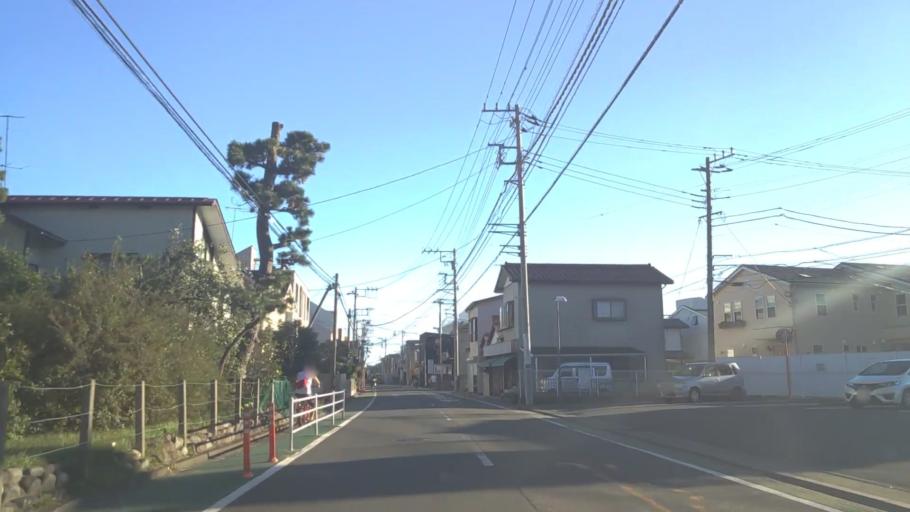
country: JP
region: Kanagawa
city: Chigasaki
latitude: 35.3297
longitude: 139.4145
